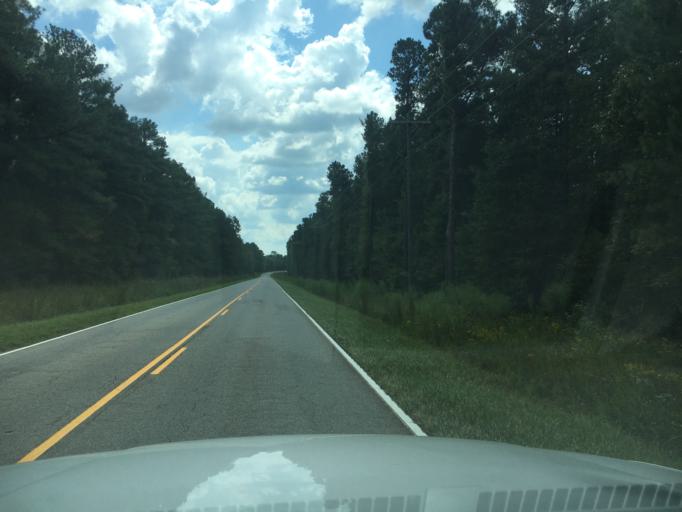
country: US
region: South Carolina
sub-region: Greenwood County
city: Greenwood
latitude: 34.0891
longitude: -82.1312
